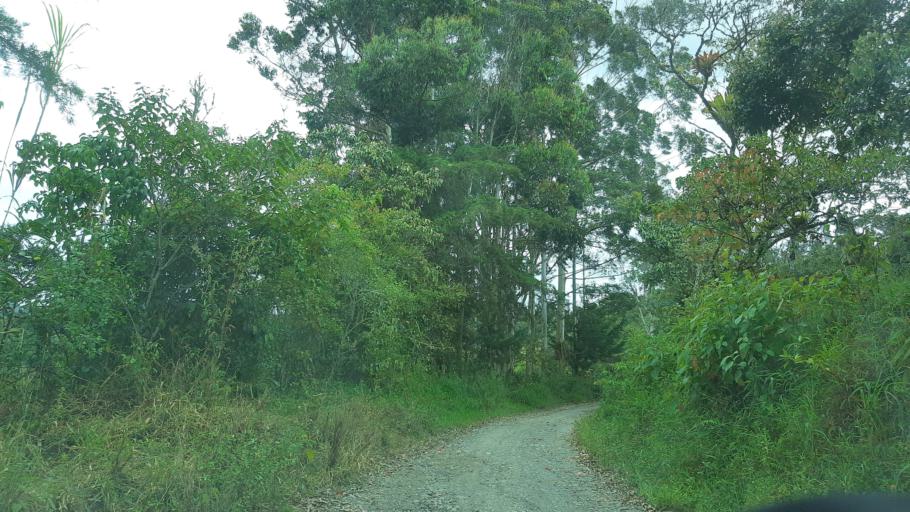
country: CO
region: Boyaca
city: Garagoa
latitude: 5.0340
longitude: -73.3308
